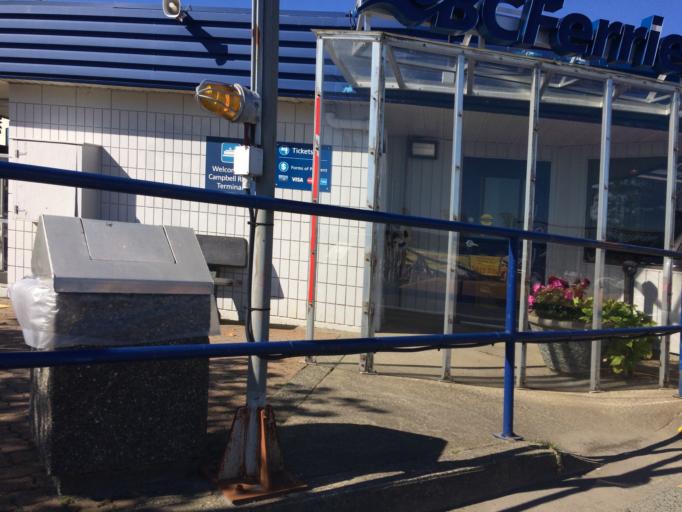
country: CA
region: British Columbia
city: Campbell River
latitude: 50.0271
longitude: -125.2416
